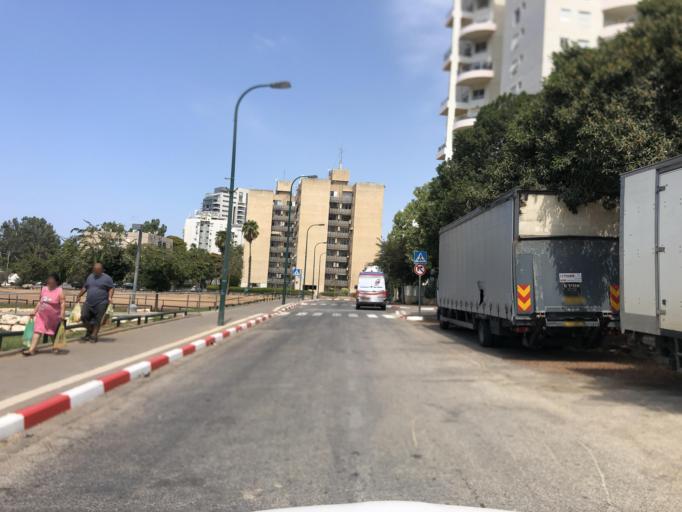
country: IL
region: Tel Aviv
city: Azor
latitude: 32.0435
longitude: 34.8002
